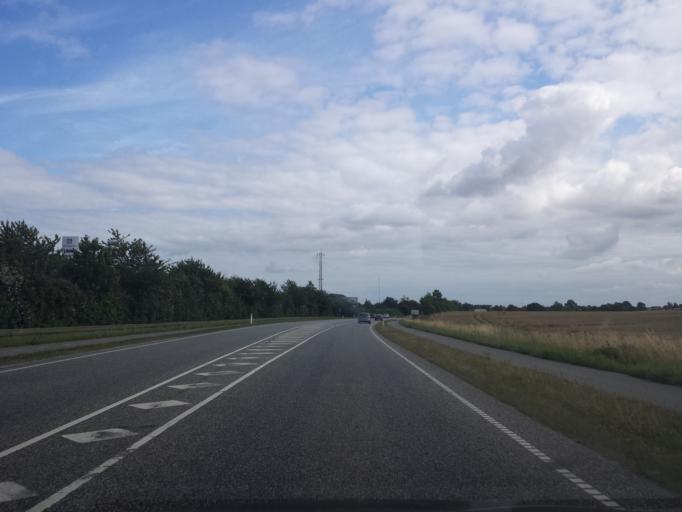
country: DK
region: South Denmark
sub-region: Sonderborg Kommune
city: Guderup
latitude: 54.9965
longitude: 9.8541
